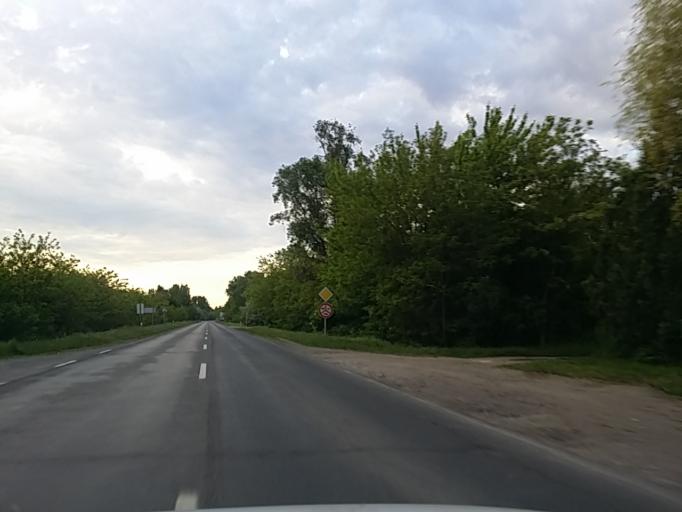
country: HU
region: Bacs-Kiskun
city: Lajosmizse
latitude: 46.9975
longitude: 19.5995
